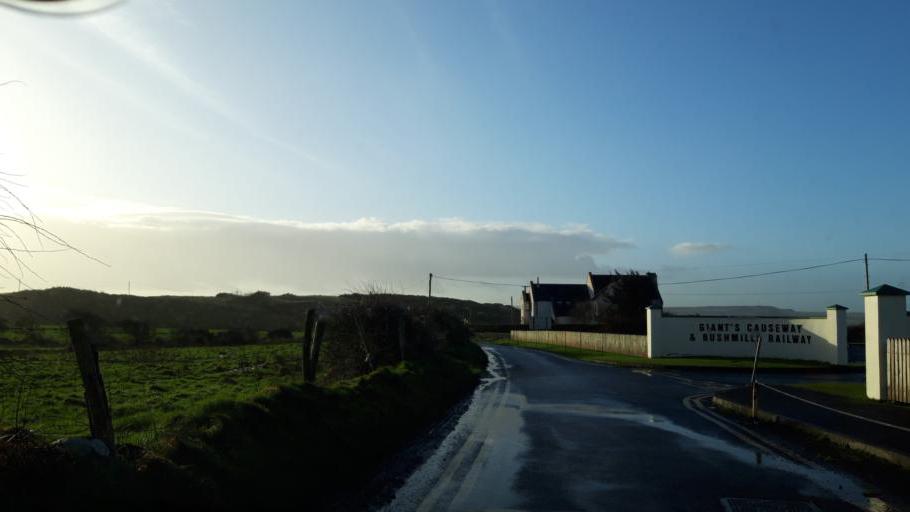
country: GB
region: Northern Ireland
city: Bushmills
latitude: 55.2308
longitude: -6.5180
